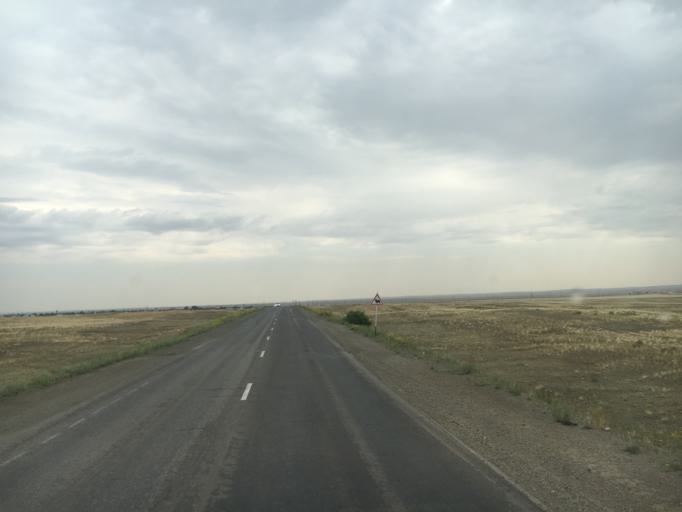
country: KZ
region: Aqtoebe
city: Khromtau
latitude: 50.2447
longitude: 58.4784
